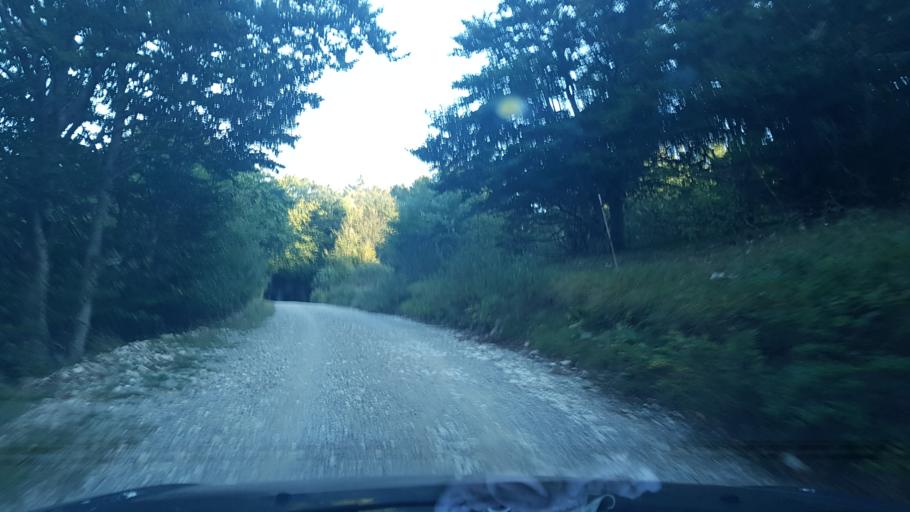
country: SI
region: Vipava
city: Vipava
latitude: 45.7778
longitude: 14.0452
